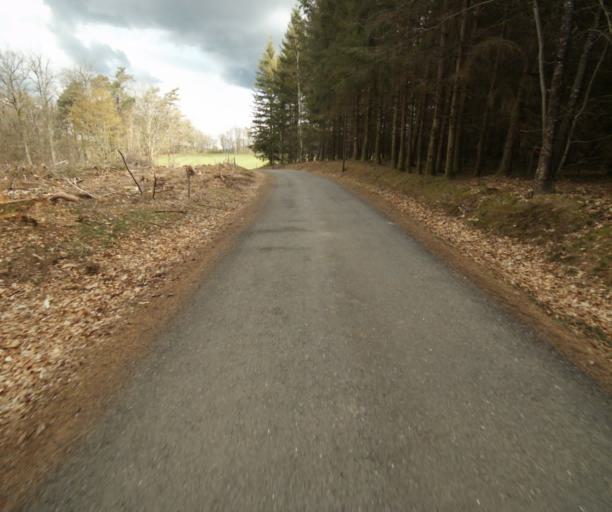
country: FR
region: Limousin
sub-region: Departement de la Correze
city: Laguenne
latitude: 45.2479
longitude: 1.9100
